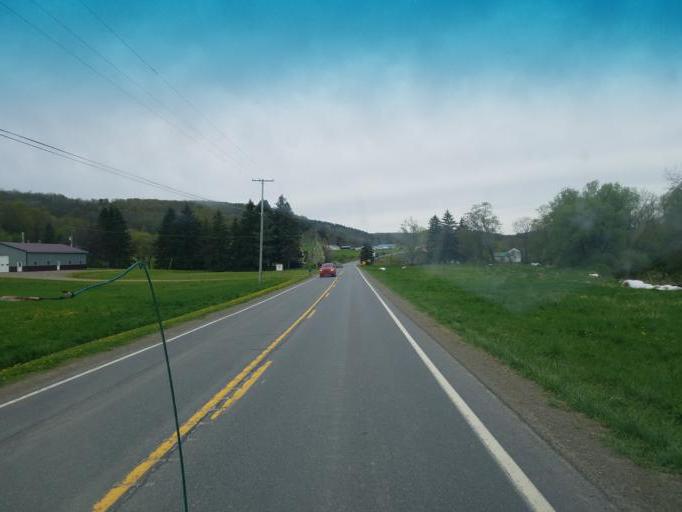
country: US
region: Pennsylvania
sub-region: Tioga County
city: Westfield
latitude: 41.8911
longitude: -77.5304
